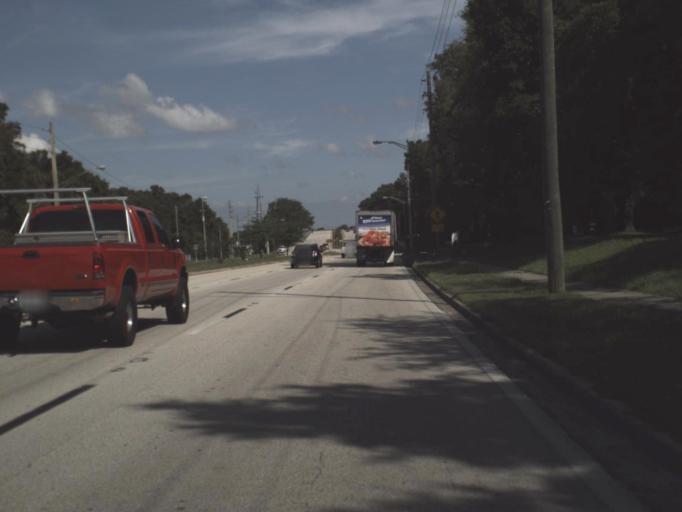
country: US
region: Florida
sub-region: Duval County
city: Jacksonville
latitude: 30.2701
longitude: -81.7124
